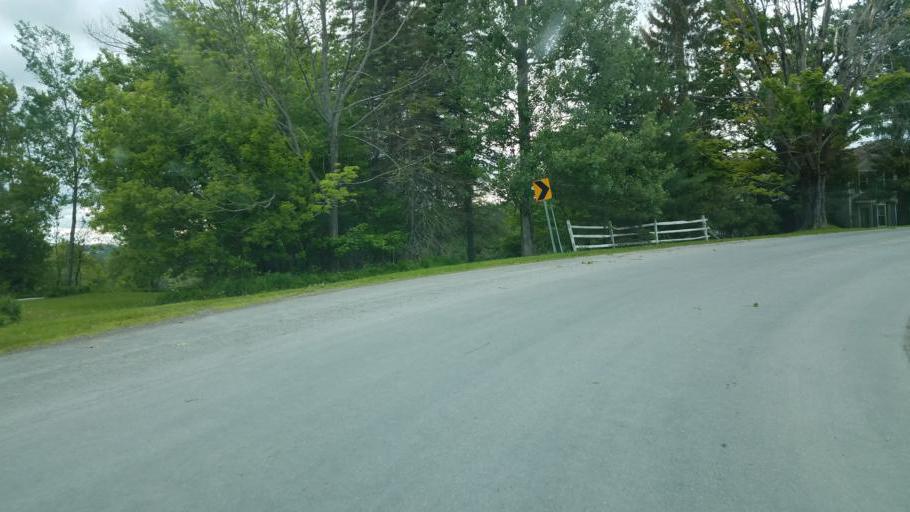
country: US
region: New York
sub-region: Otsego County
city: Richfield Springs
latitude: 42.8457
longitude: -74.9665
